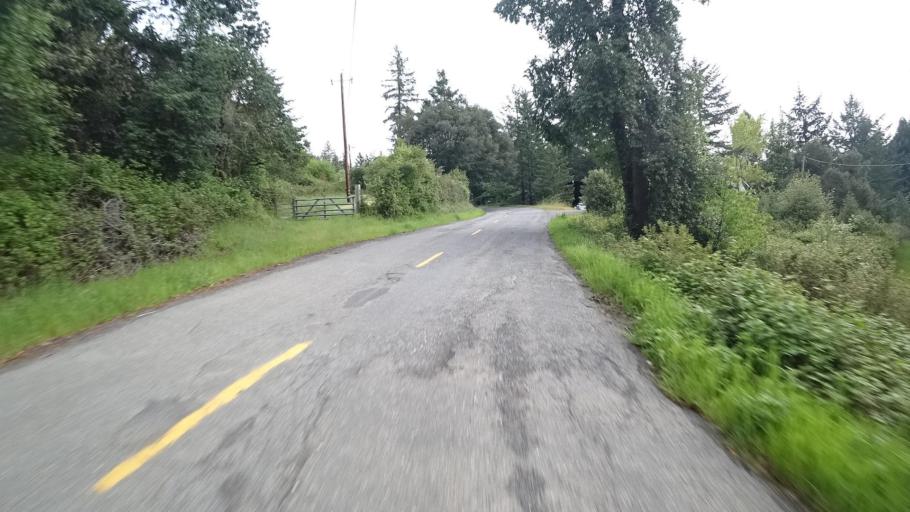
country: US
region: California
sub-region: Humboldt County
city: Redway
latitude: 40.3019
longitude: -123.8221
